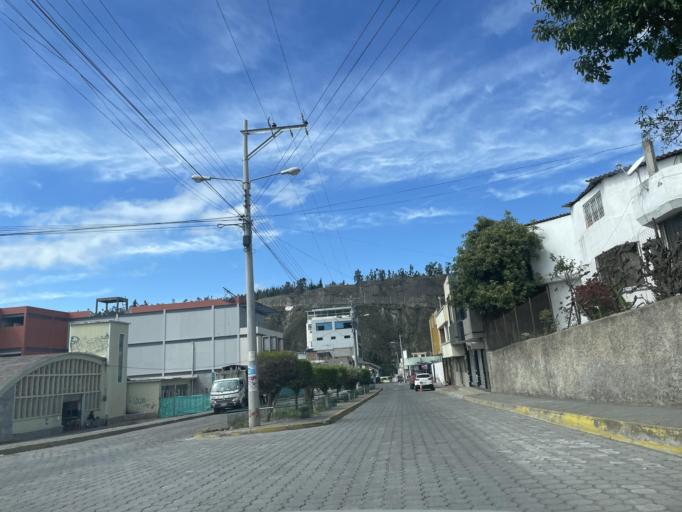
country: EC
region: Chimborazo
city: Guano
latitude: -1.6058
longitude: -78.6428
